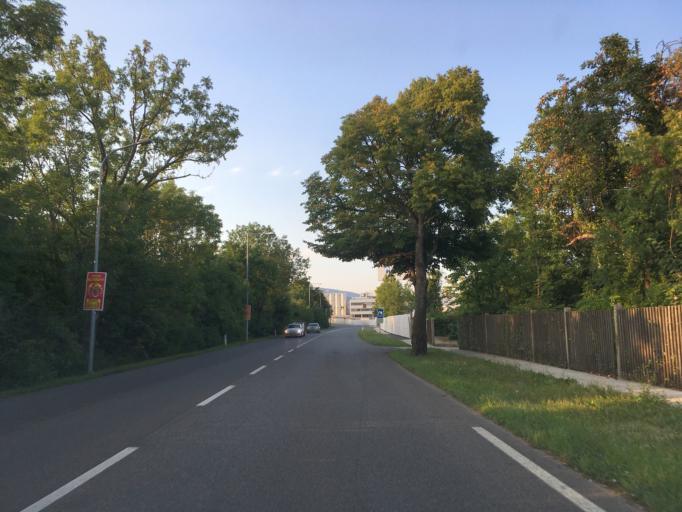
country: AT
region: Lower Austria
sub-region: Politischer Bezirk Baden
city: Baden
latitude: 47.9884
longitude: 16.2242
